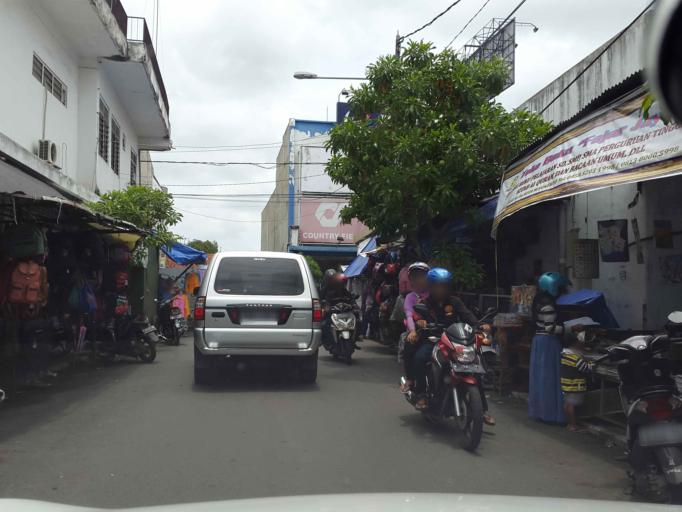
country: ID
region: East Java
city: Mojokerto
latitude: -7.4667
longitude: 112.4325
